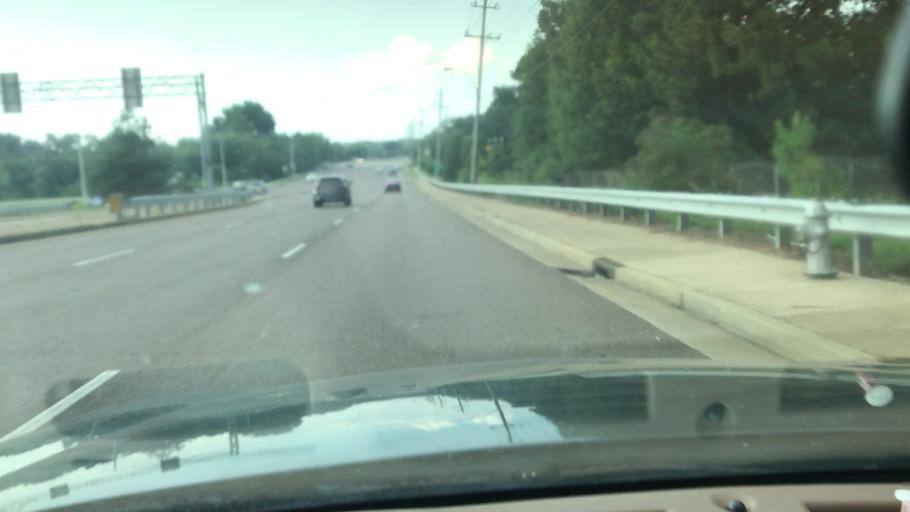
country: US
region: Tennessee
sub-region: Shelby County
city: Bartlett
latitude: 35.1874
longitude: -89.8136
